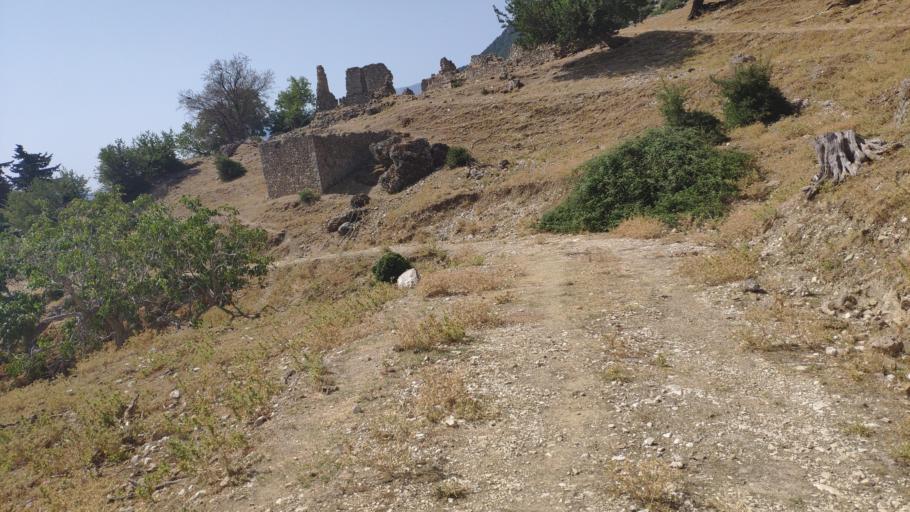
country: GR
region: West Greece
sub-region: Nomos Aitolias kai Akarnanias
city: Monastirakion
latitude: 38.8152
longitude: 21.0172
